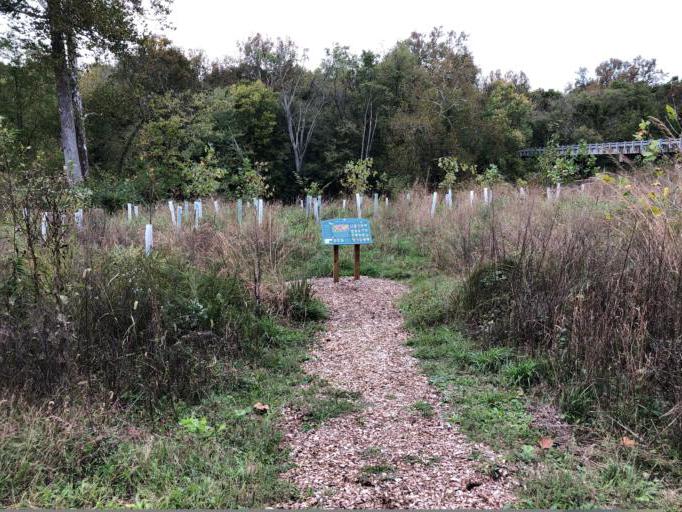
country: US
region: Ohio
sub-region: Warren County
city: Kings Mills
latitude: 39.3511
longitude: -84.2430
